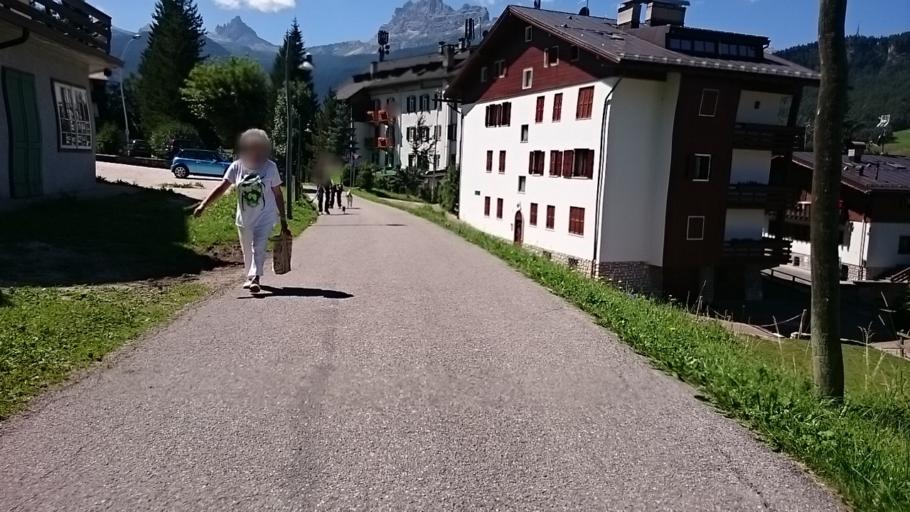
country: IT
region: Veneto
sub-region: Provincia di Belluno
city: Cortina d'Ampezzo
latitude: 46.5332
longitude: 12.1420
